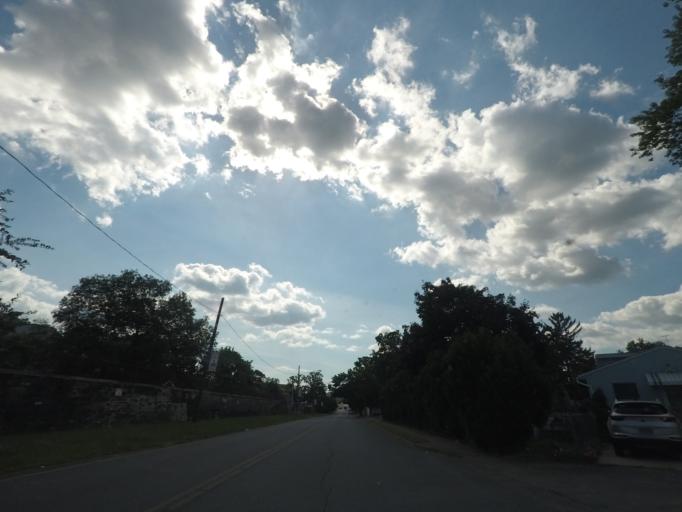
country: US
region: New York
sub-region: Albany County
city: Watervliet
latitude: 42.7230
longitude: -73.7053
